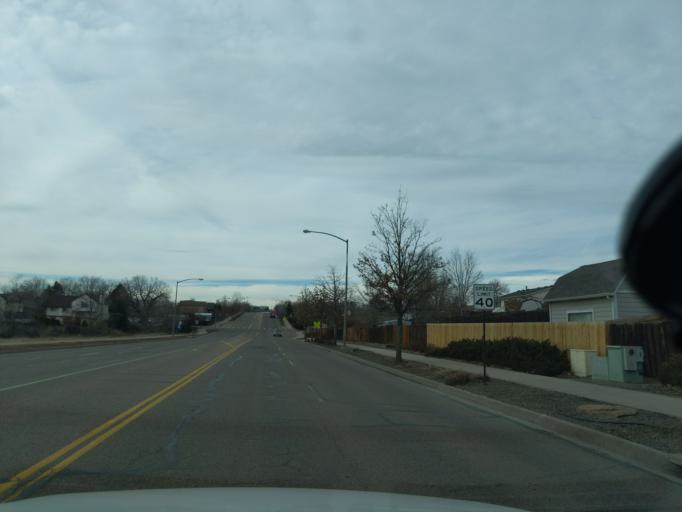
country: US
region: Colorado
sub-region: Adams County
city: Thornton
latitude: 39.8705
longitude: -104.9496
